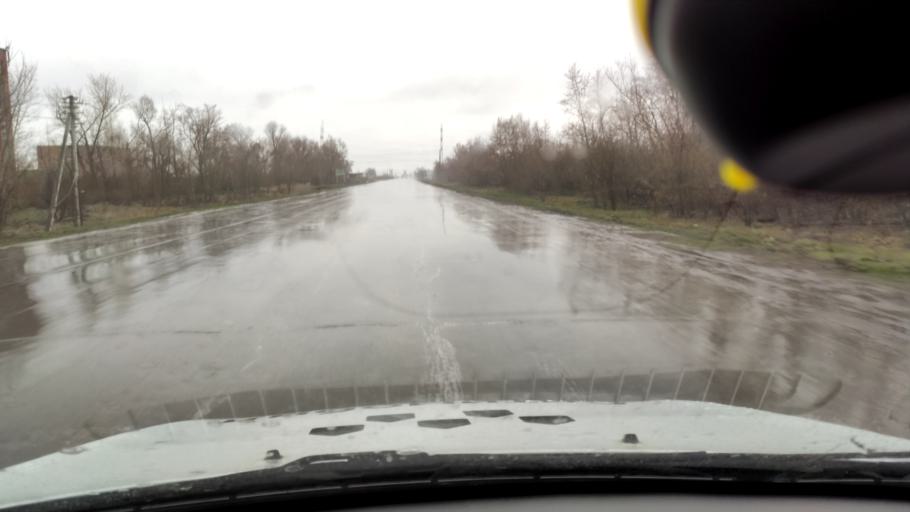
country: RU
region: Samara
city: Tol'yatti
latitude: 53.5856
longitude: 49.4048
